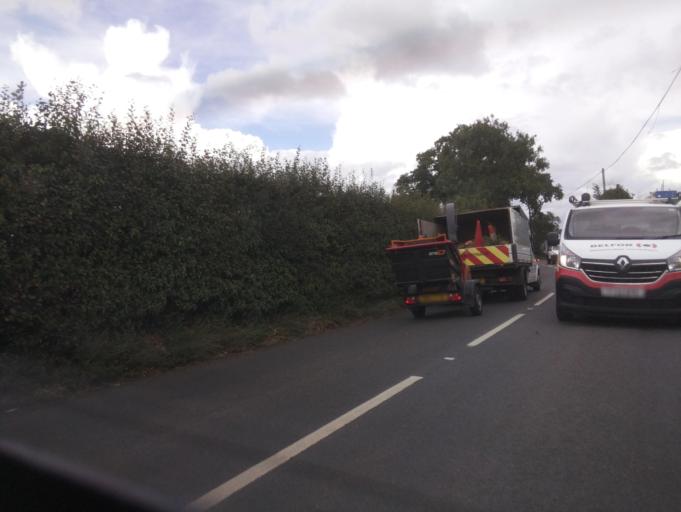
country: GB
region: England
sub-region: Telford and Wrekin
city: Newport
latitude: 52.7973
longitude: -2.3480
